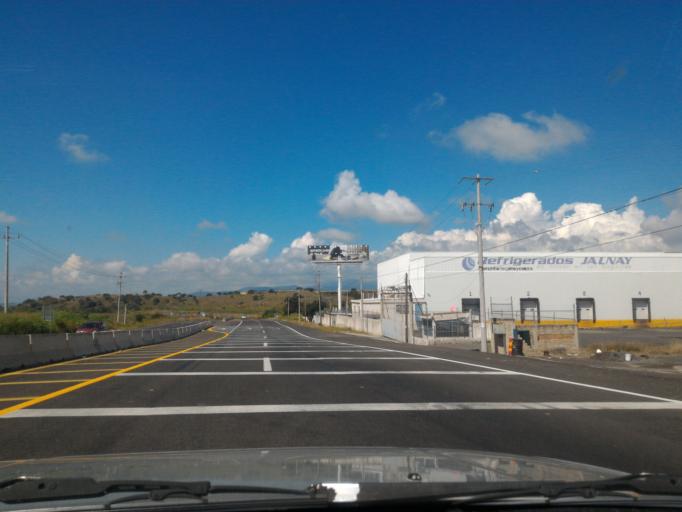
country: MX
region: Jalisco
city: La Venta del Astillero
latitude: 20.7320
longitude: -103.6144
